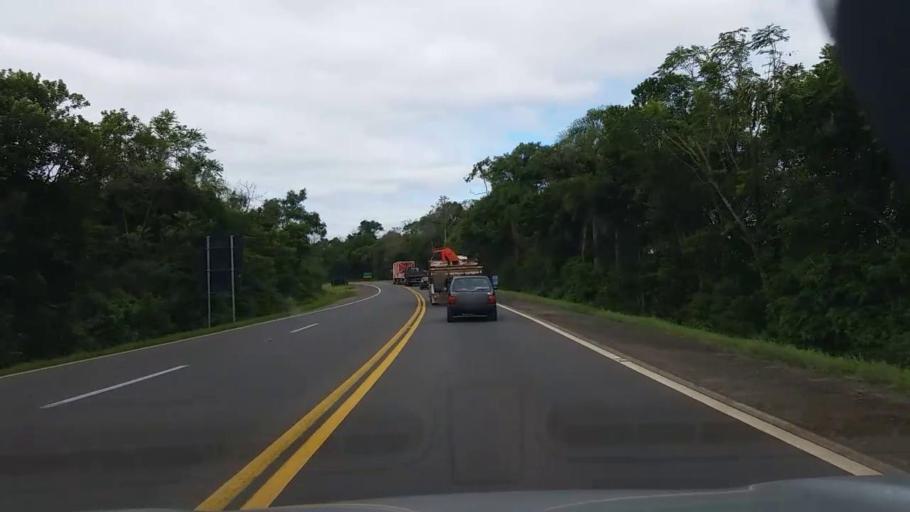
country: BR
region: Rio Grande do Sul
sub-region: Arroio Do Meio
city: Arroio do Meio
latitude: -29.3999
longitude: -52.0406
